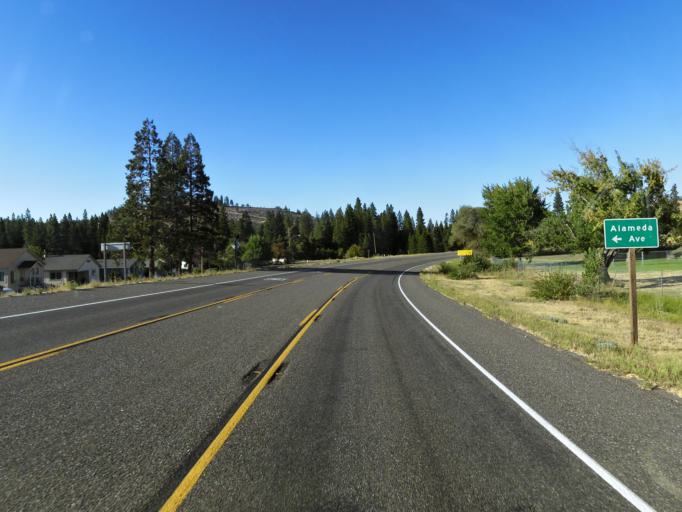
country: US
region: California
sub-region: Siskiyou County
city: Weed
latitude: 41.4376
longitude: -122.3873
